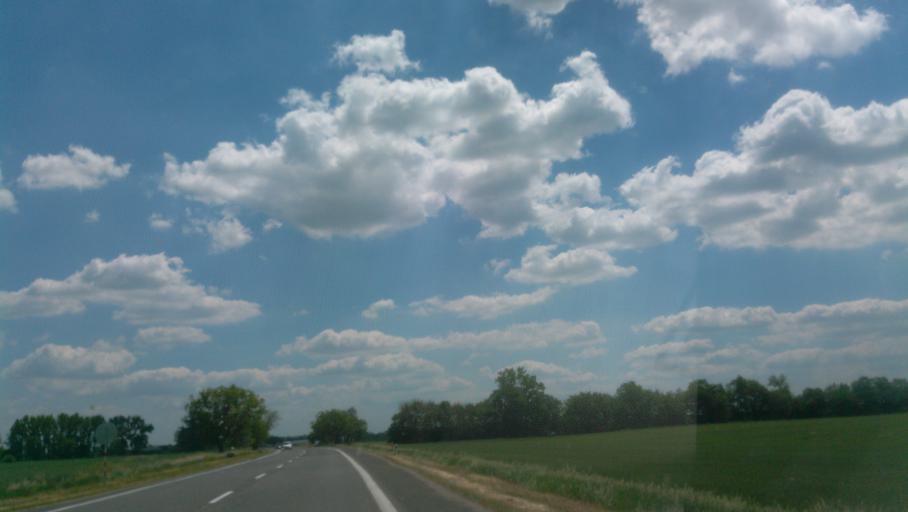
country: SK
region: Bratislavsky
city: Dunajska Luzna
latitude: 48.0603
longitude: 17.2828
